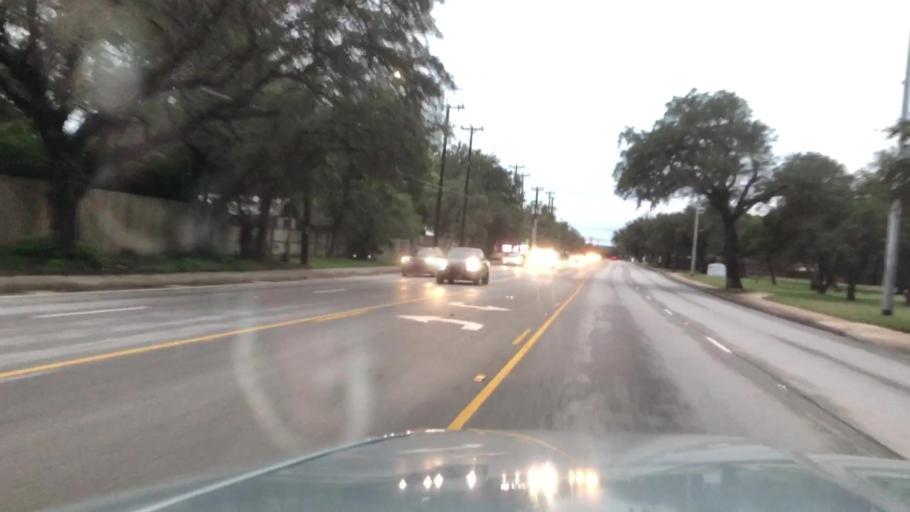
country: US
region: Texas
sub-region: Bexar County
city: Shavano Park
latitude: 29.5631
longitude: -98.6071
